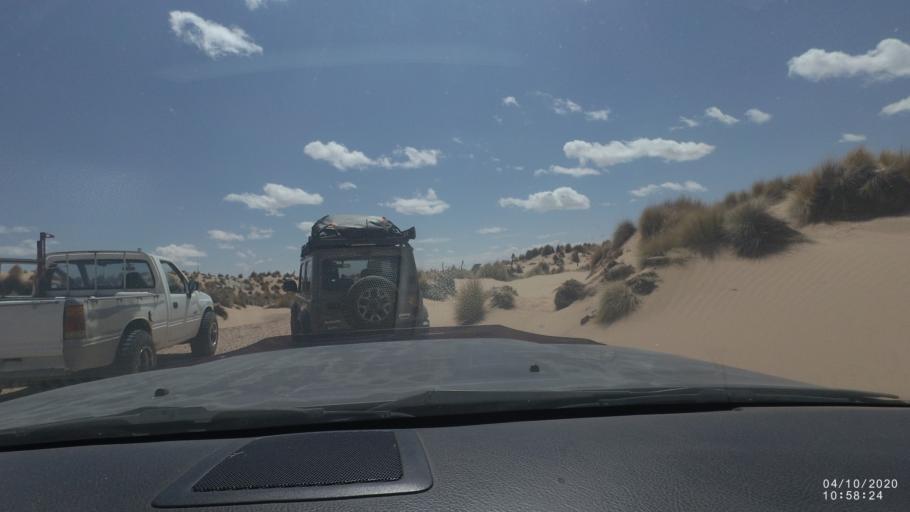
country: BO
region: Oruro
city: Poopo
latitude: -18.7009
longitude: -67.4673
